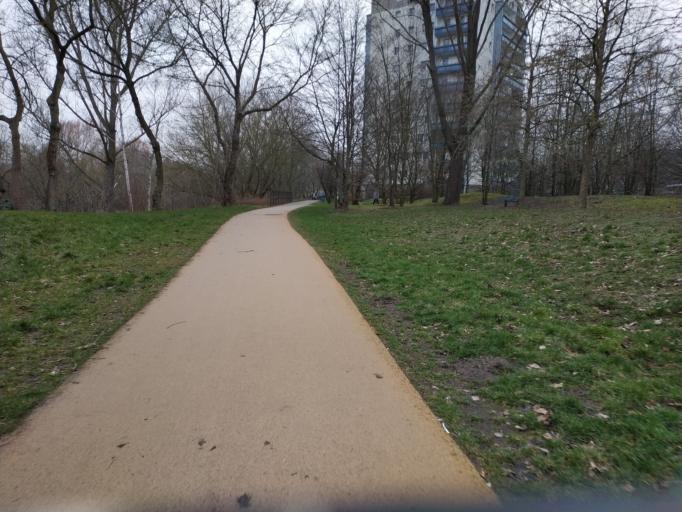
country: DE
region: Berlin
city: Marzahn
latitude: 52.5382
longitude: 13.5854
